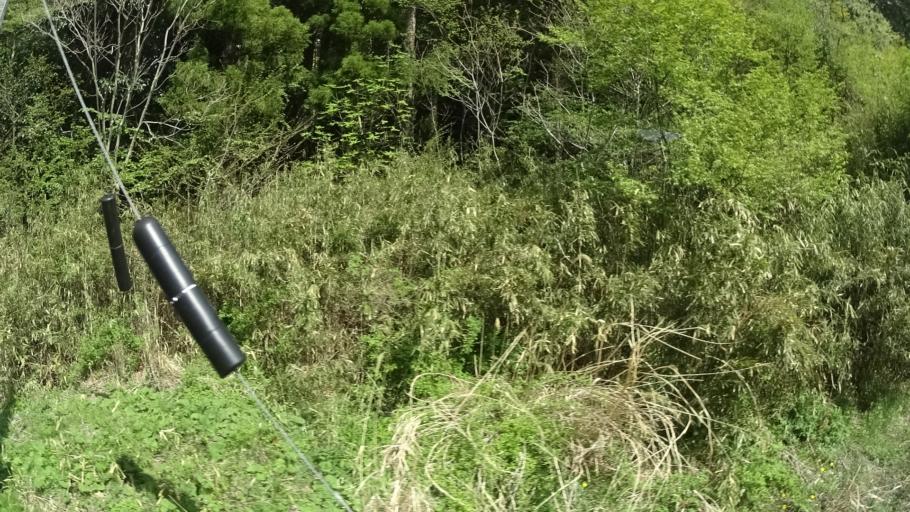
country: JP
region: Fukushima
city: Namie
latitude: 37.5731
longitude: 140.9974
